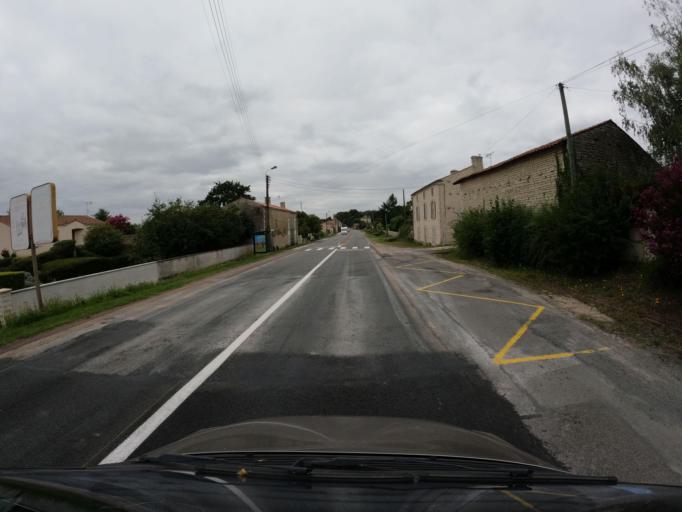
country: FR
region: Pays de la Loire
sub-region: Departement de la Vendee
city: Benet
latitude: 46.3973
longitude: -0.6554
